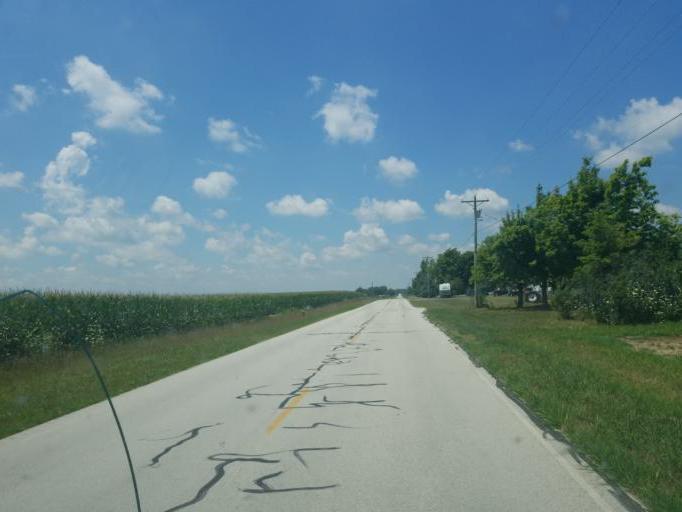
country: US
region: Ohio
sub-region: Allen County
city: Spencerville
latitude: 40.6772
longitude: -84.4798
